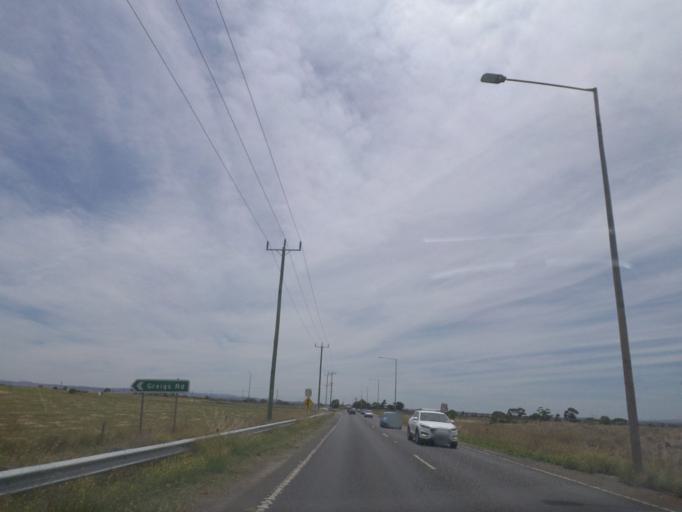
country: AU
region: Victoria
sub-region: Melton
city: Caroline Springs
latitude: -37.7545
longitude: 144.7036
